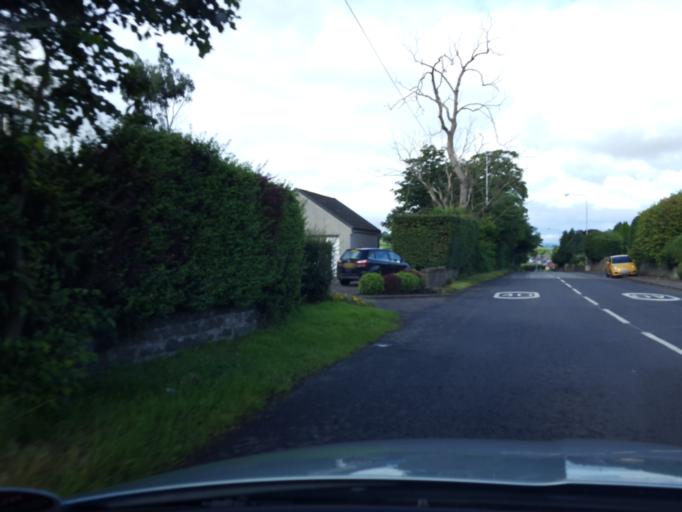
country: GB
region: Scotland
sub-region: West Lothian
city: Linlithgow
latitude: 55.9750
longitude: -3.5719
